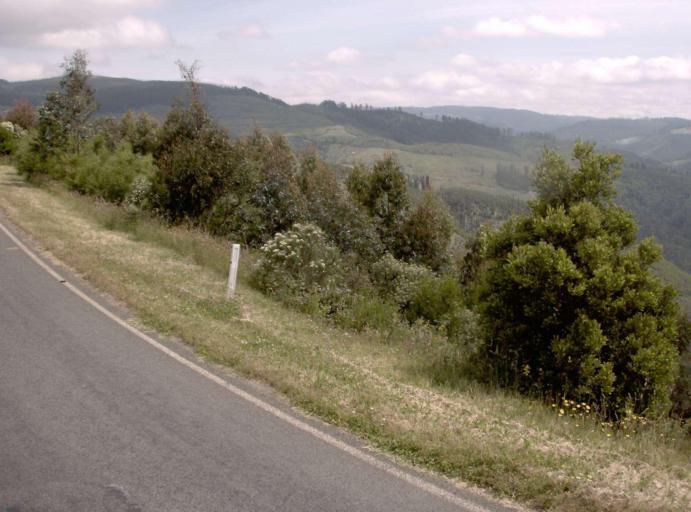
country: AU
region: Victoria
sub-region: Latrobe
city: Traralgon
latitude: -38.3621
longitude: 146.5640
